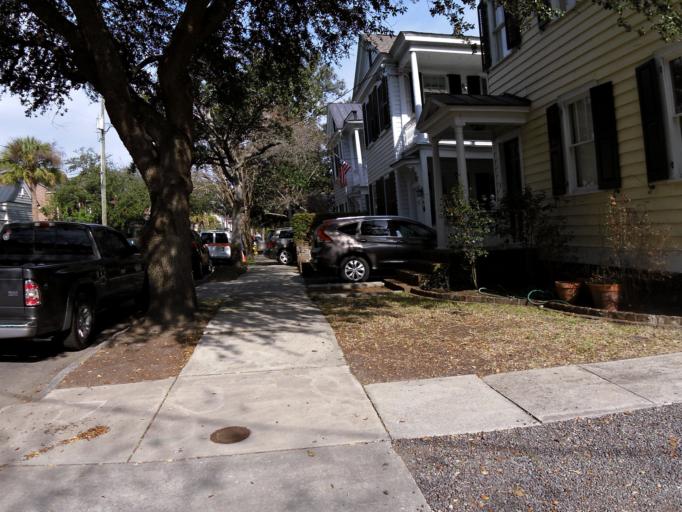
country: US
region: South Carolina
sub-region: Charleston County
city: Charleston
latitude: 32.7726
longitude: -79.9379
